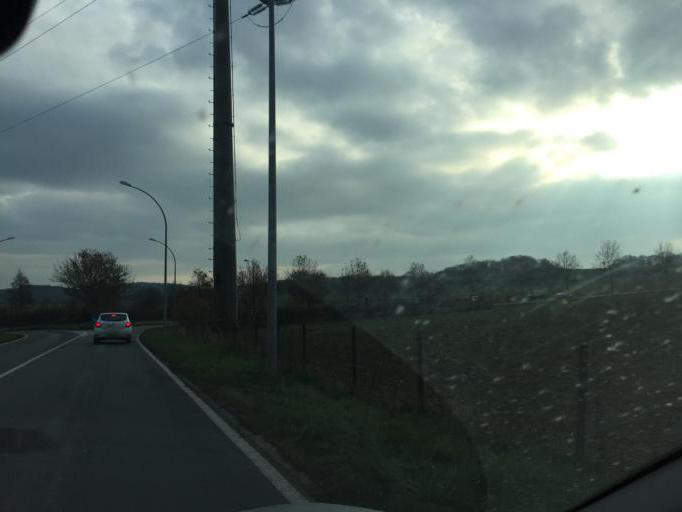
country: LU
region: Diekirch
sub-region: Canton de Redange
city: Useldange
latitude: 49.7560
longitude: 5.9585
